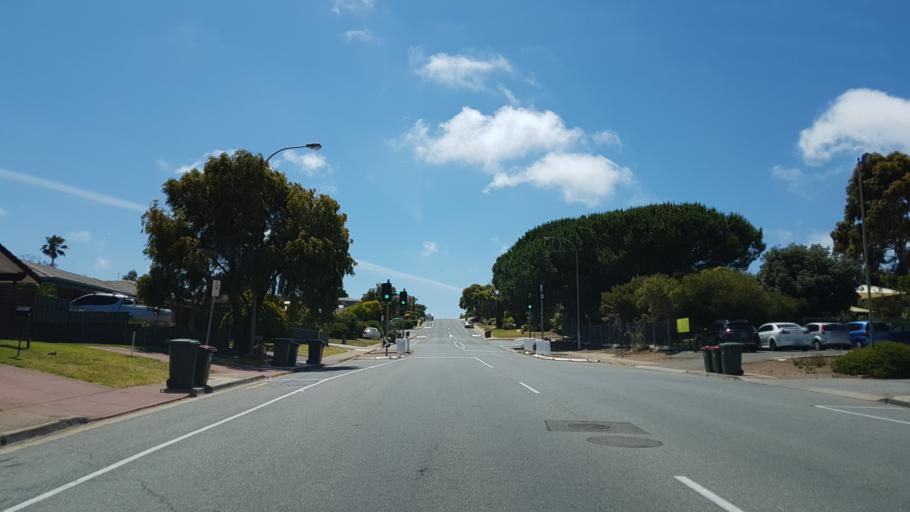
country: AU
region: South Australia
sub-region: Marion
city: Happy Valley
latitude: -35.0679
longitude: 138.5178
